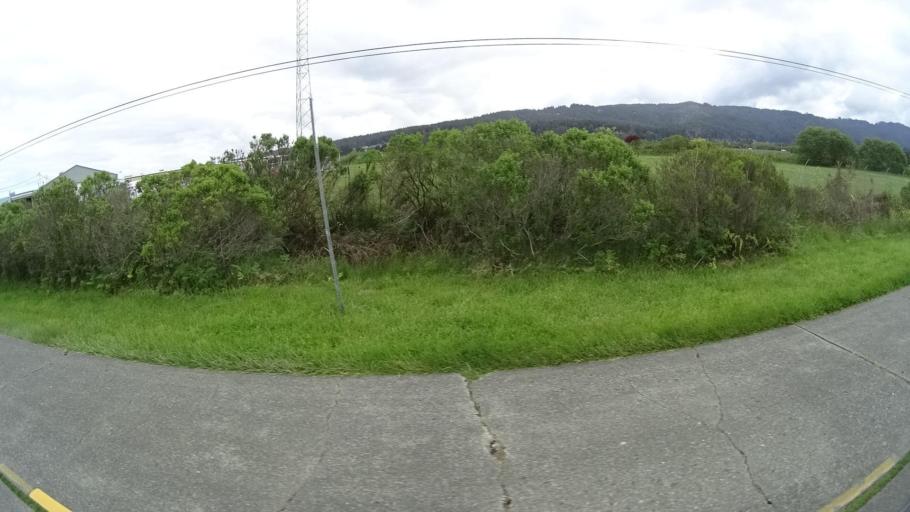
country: US
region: California
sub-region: Humboldt County
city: Arcata
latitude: 40.8554
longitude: -124.0888
